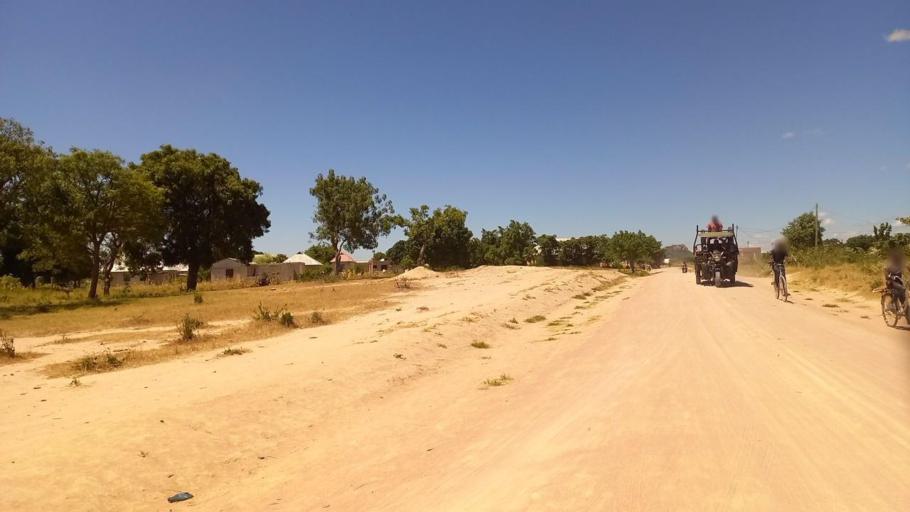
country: TZ
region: Dodoma
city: Dodoma
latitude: -6.1306
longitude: 35.7318
